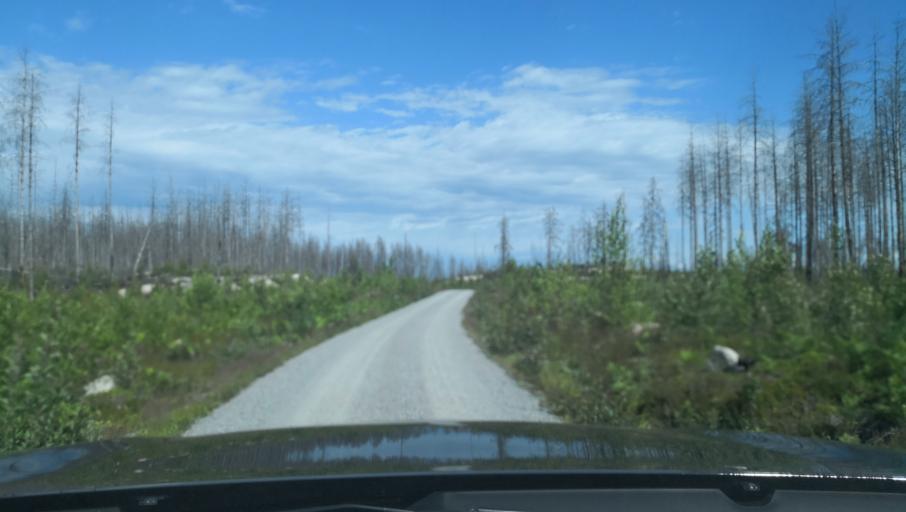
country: SE
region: Vaestmanland
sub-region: Surahammars Kommun
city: Ramnas
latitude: 59.9292
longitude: 16.1739
